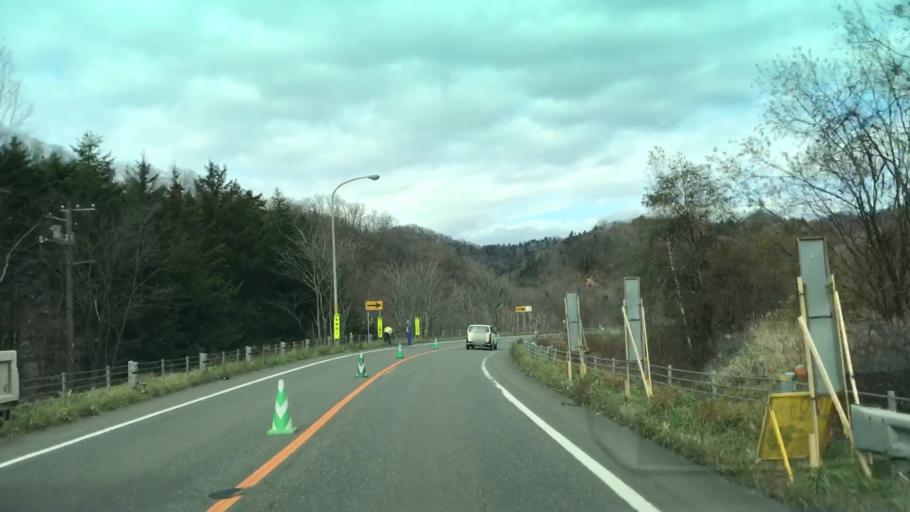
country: JP
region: Hokkaido
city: Shizunai-furukawacho
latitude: 42.7928
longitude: 142.3934
